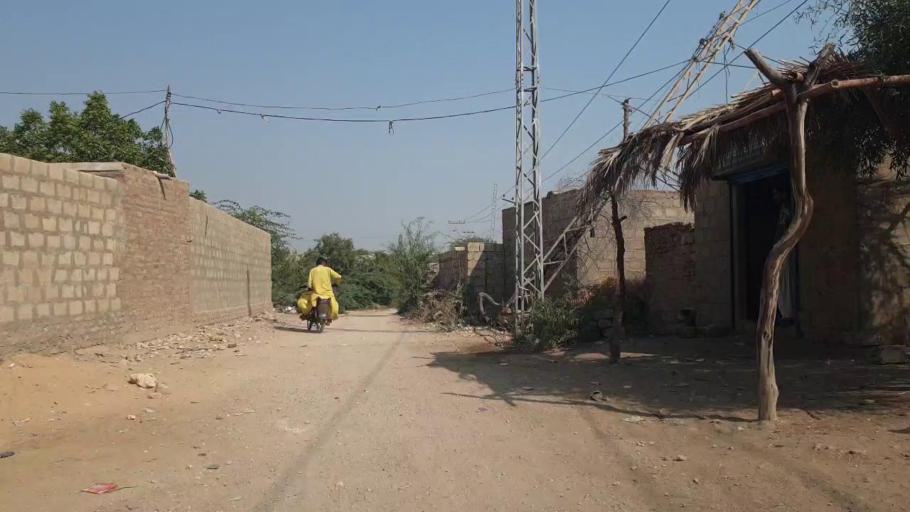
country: PK
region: Sindh
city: Kotri
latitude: 25.3377
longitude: 68.2804
